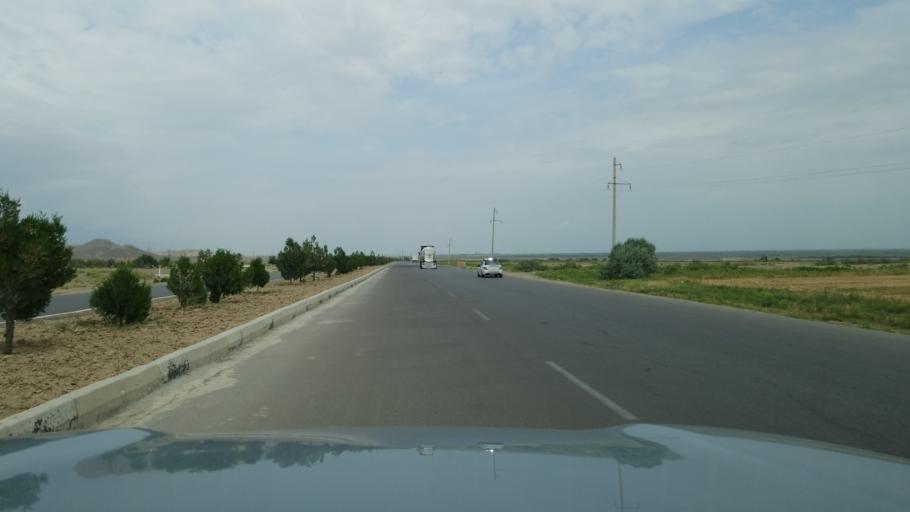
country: TM
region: Ahal
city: Baharly
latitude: 38.2384
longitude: 57.7714
